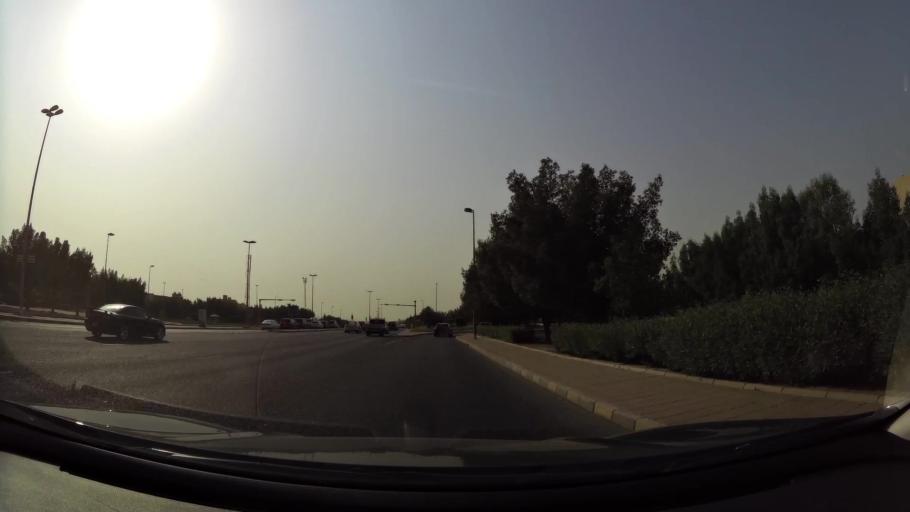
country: KW
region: Mubarak al Kabir
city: Mubarak al Kabir
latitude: 29.2095
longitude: 48.0796
